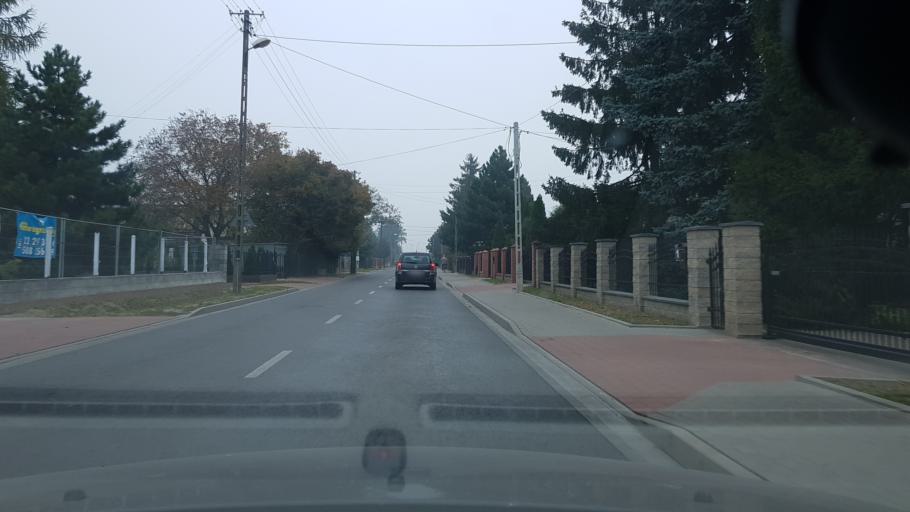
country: PL
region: Masovian Voivodeship
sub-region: Powiat pruszkowski
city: Piastow
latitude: 52.2118
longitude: 20.8397
